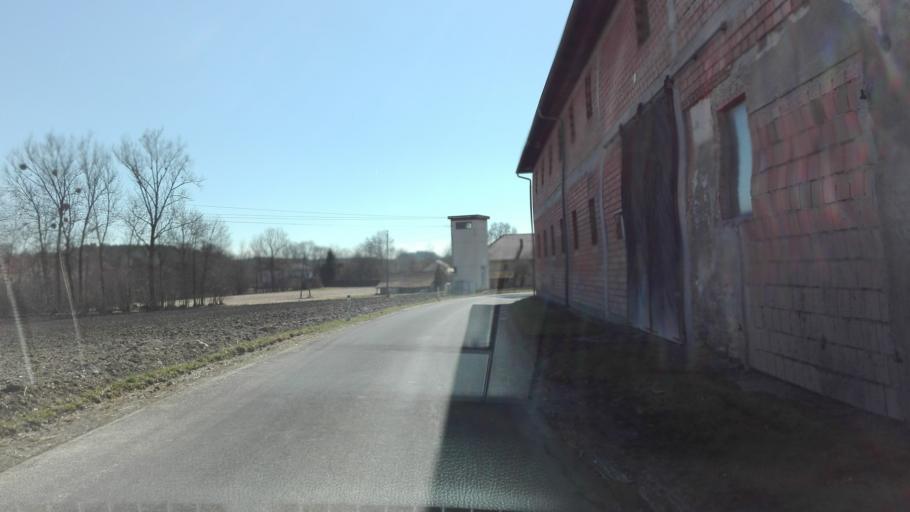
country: AT
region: Upper Austria
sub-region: Wels-Land
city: Buchkirchen
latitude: 48.2175
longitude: 13.9724
